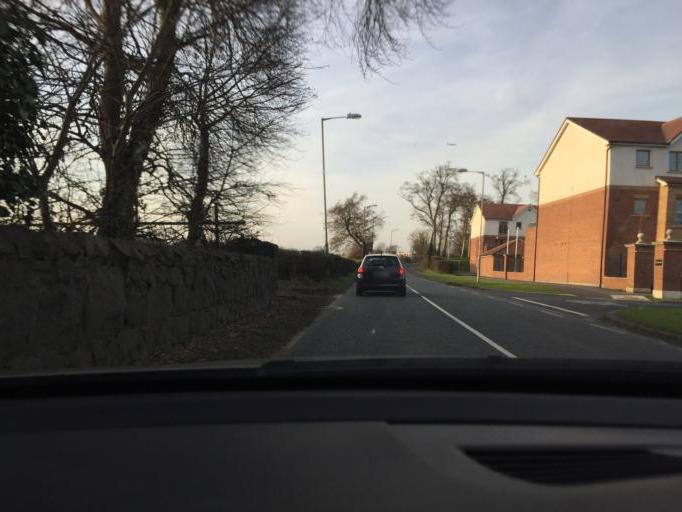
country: IE
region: Leinster
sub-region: An Mhi
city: Dunboyne
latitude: 53.4068
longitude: -6.4457
